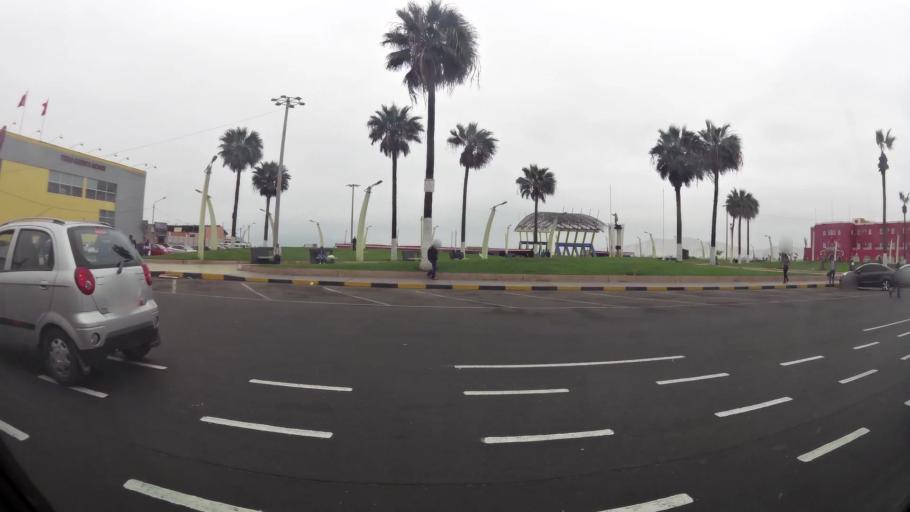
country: PE
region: Ancash
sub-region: Provincia de Santa
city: Chimbote
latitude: -9.0778
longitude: -78.5896
